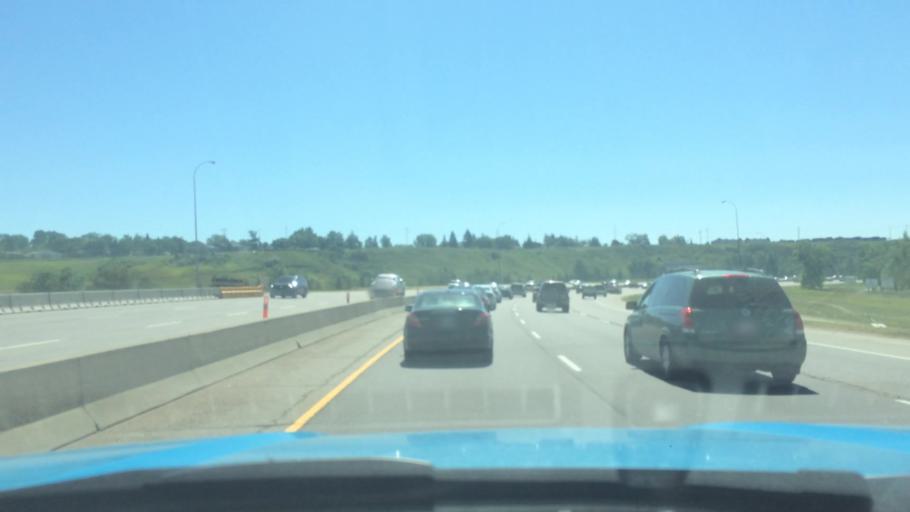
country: CA
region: Alberta
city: Calgary
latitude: 51.0354
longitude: -114.0007
